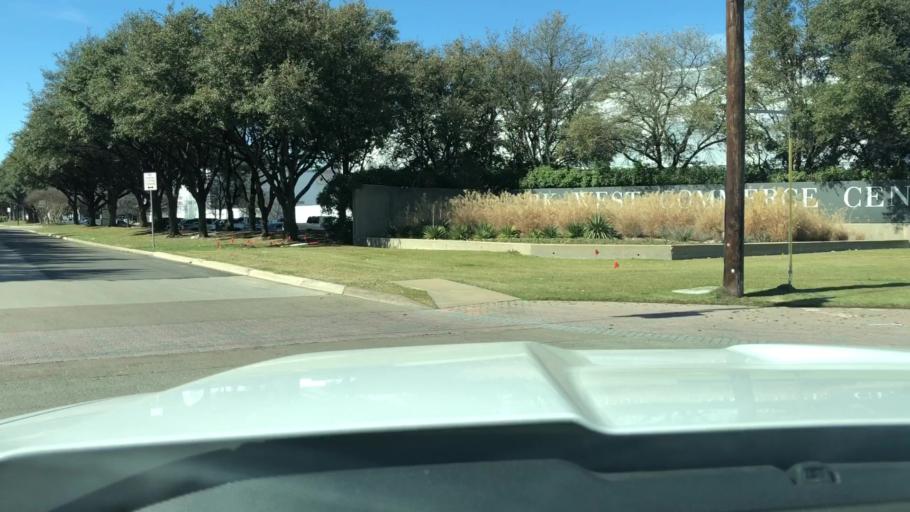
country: US
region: Texas
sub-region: Dallas County
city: Coppell
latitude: 32.9437
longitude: -96.9936
